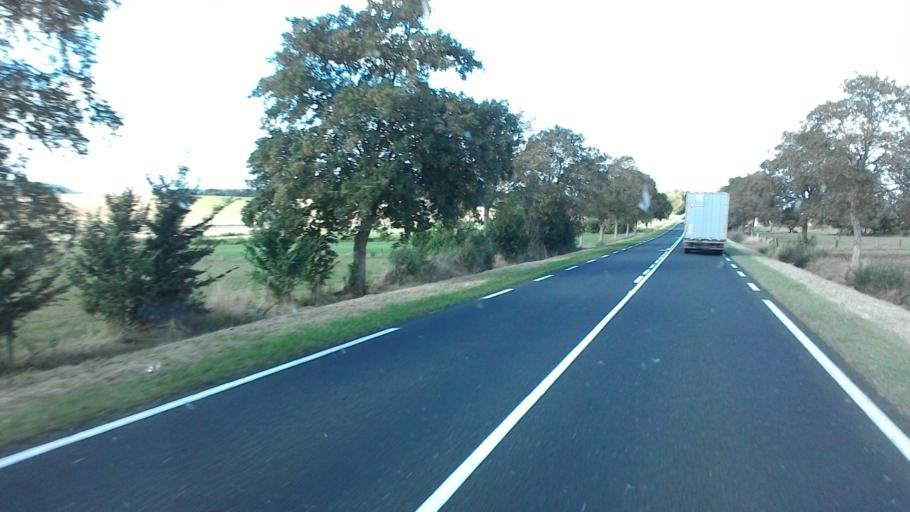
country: FR
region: Lorraine
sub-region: Departement de Meurthe-et-Moselle
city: Colombey-les-Belles
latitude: 48.5692
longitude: 5.8890
